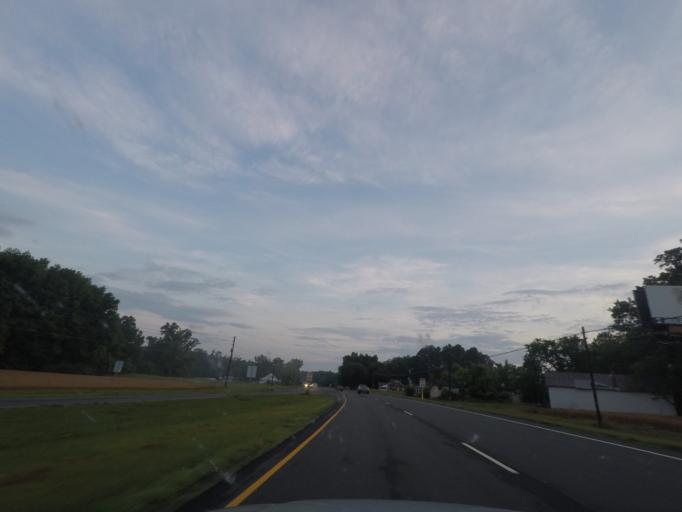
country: US
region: North Carolina
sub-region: Person County
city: Roxboro
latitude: 36.2739
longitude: -78.9469
